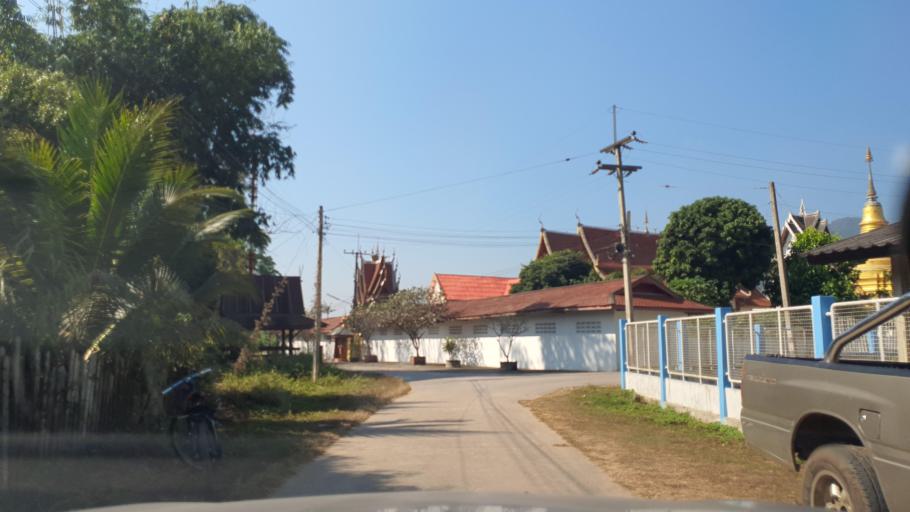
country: TH
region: Lamphun
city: Mae Tha
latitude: 18.5439
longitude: 99.2447
